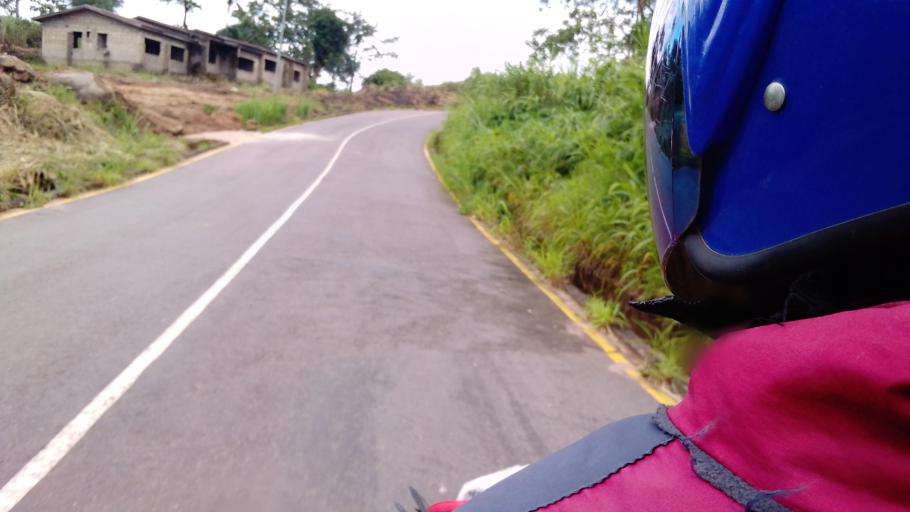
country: SL
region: Eastern Province
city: Koidu
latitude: 8.6579
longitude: -10.9864
